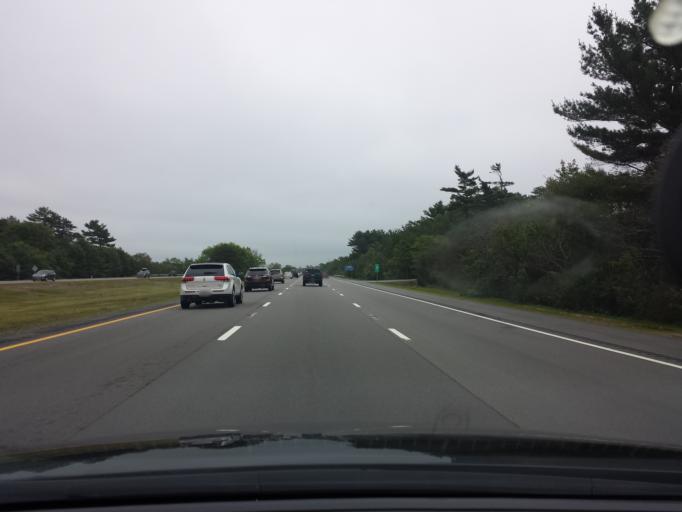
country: US
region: Massachusetts
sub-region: Plymouth County
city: Onset
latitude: 41.7674
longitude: -70.6799
